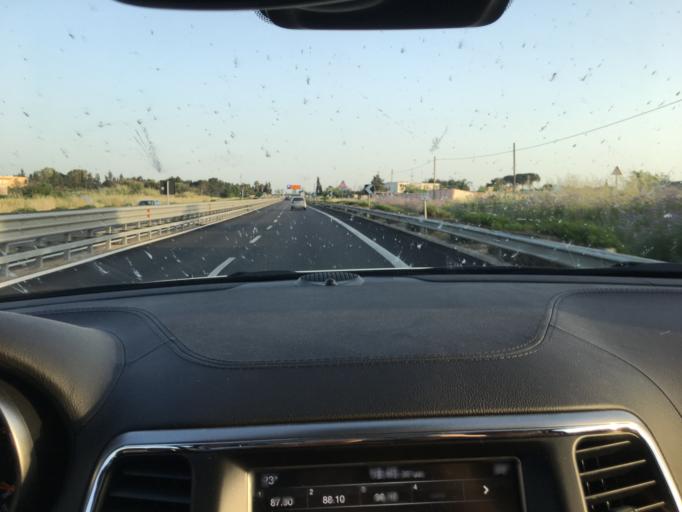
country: IT
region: Apulia
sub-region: Provincia di Lecce
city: San Pietro in Lama
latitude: 40.2969
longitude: 18.1321
